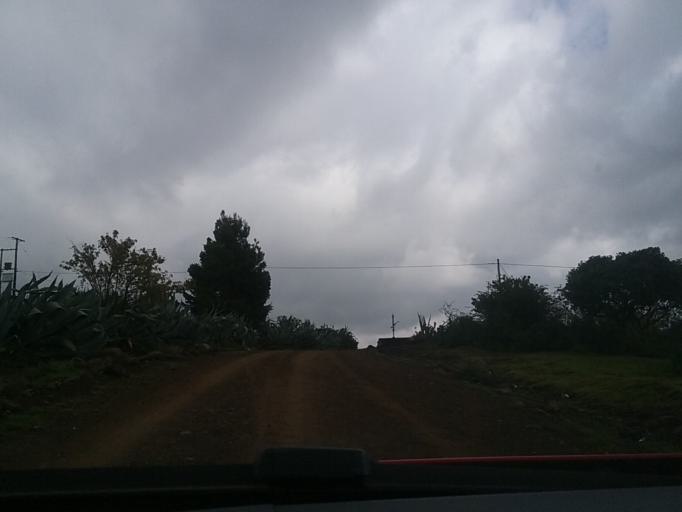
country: LS
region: Berea
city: Teyateyaneng
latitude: -29.2500
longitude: 27.8451
